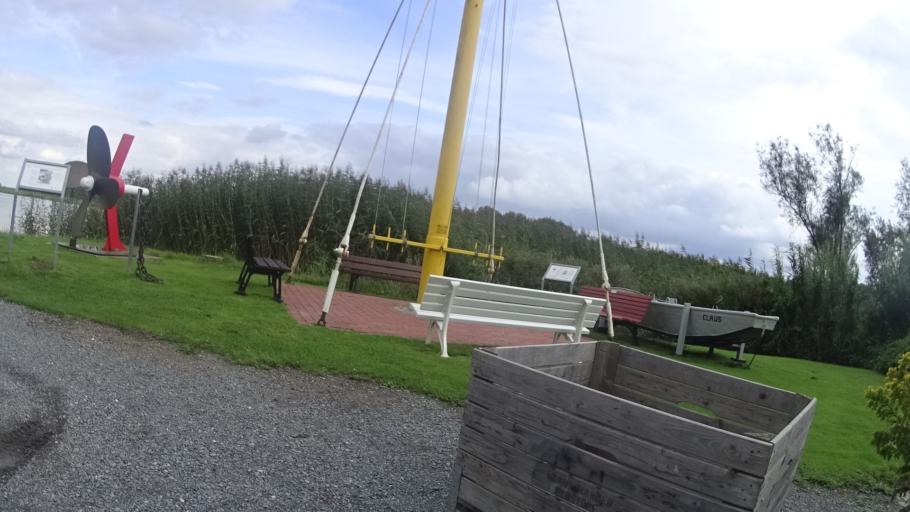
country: DE
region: Lower Saxony
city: Wischhafen
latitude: 53.7723
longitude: 9.3243
